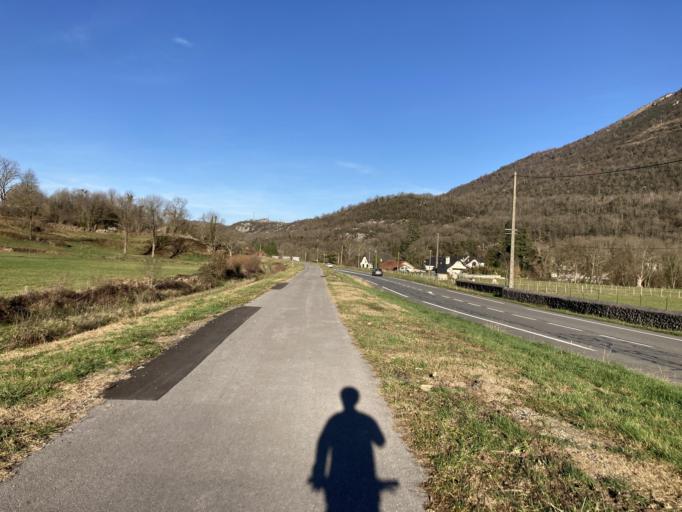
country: FR
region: Aquitaine
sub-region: Departement des Pyrenees-Atlantiques
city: Louvie-Juzon
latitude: 43.0715
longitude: -0.4224
